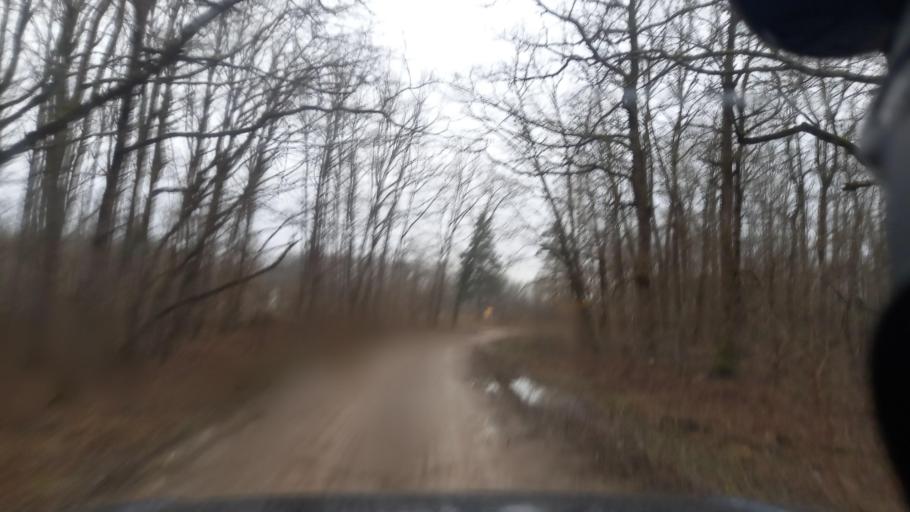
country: RU
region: Krasnodarskiy
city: Saratovskaya
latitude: 44.6618
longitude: 39.2260
